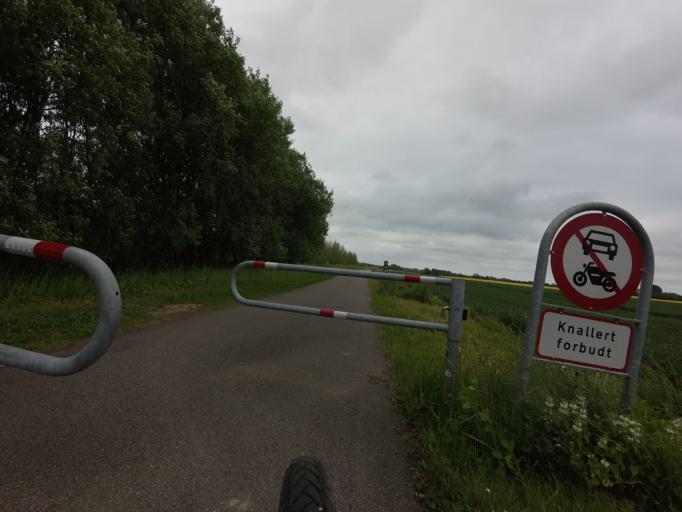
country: DK
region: Zealand
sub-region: Naestved Kommune
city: Fuglebjerg
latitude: 55.2810
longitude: 11.4244
